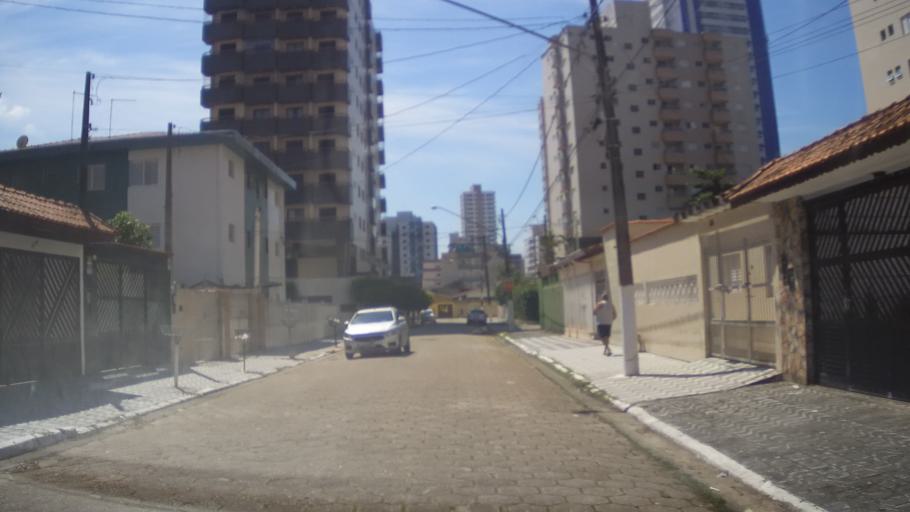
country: BR
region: Sao Paulo
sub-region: Praia Grande
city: Praia Grande
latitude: -24.0171
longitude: -46.4448
